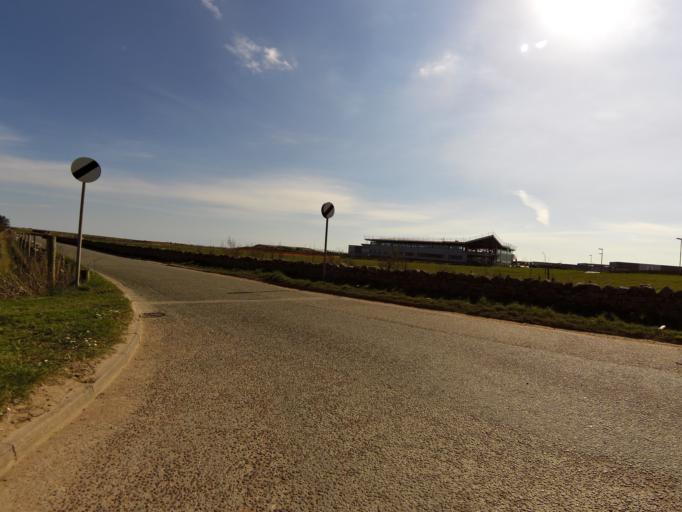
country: GB
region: Scotland
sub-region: Aberdeenshire
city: Portlethen
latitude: 57.0933
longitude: -2.1012
